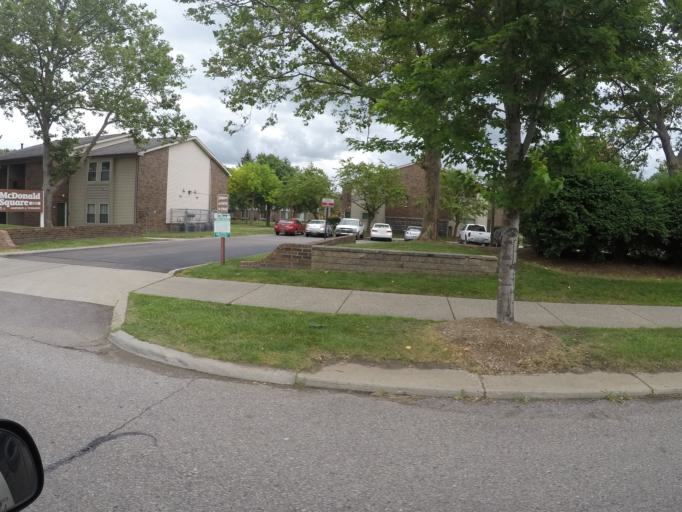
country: US
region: Michigan
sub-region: Wayne County
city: Detroit
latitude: 42.3513
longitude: -83.0268
